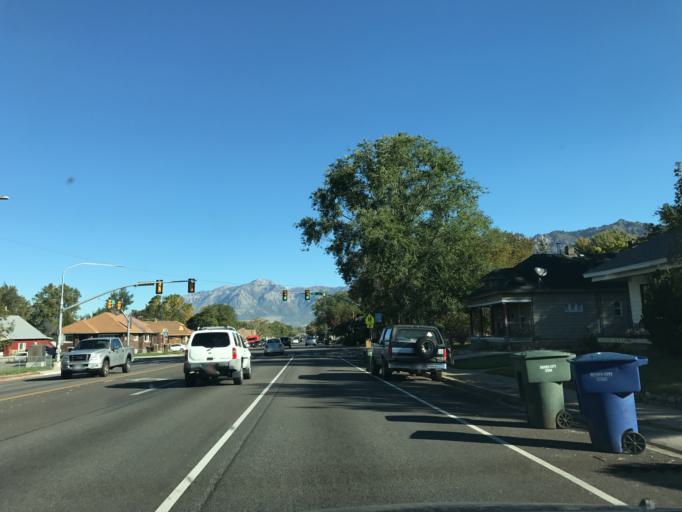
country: US
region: Utah
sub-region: Weber County
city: Ogden
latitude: 41.2177
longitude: -111.9482
